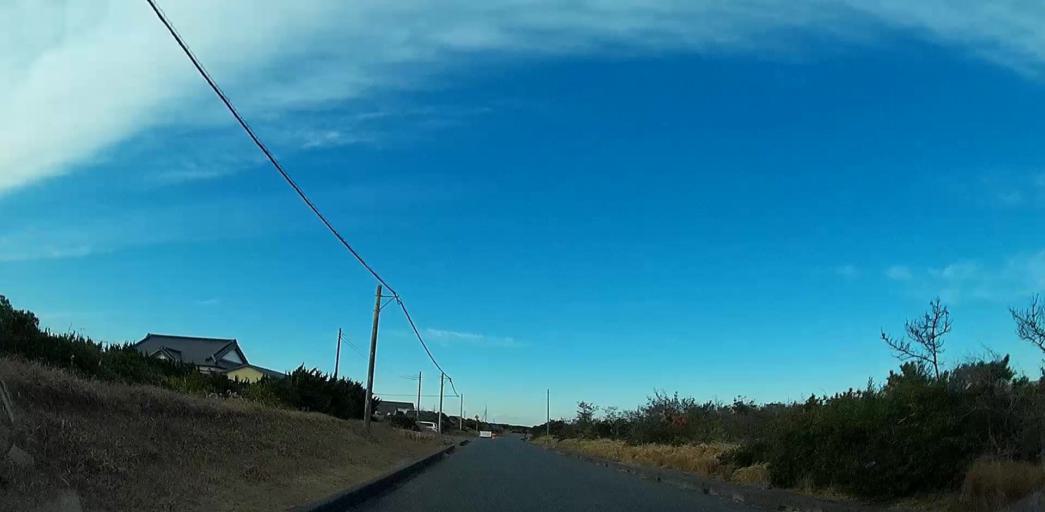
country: JP
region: Chiba
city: Hasaki
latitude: 35.7725
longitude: 140.8133
